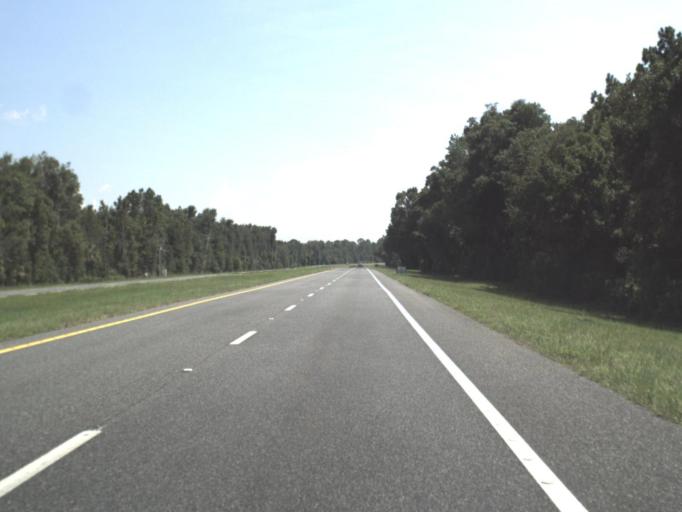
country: US
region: Florida
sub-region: Levy County
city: Inglis
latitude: 29.0994
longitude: -82.6362
